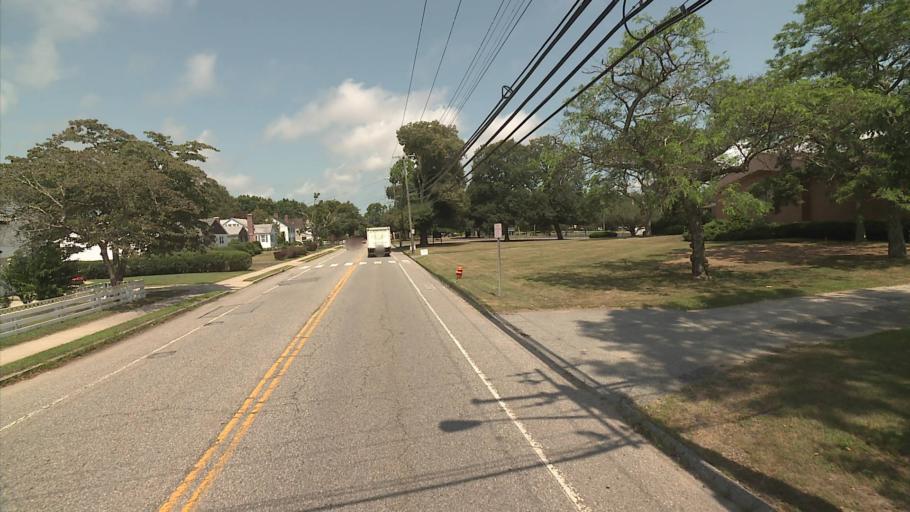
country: US
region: Connecticut
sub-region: New London County
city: New London
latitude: 41.3269
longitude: -72.1020
